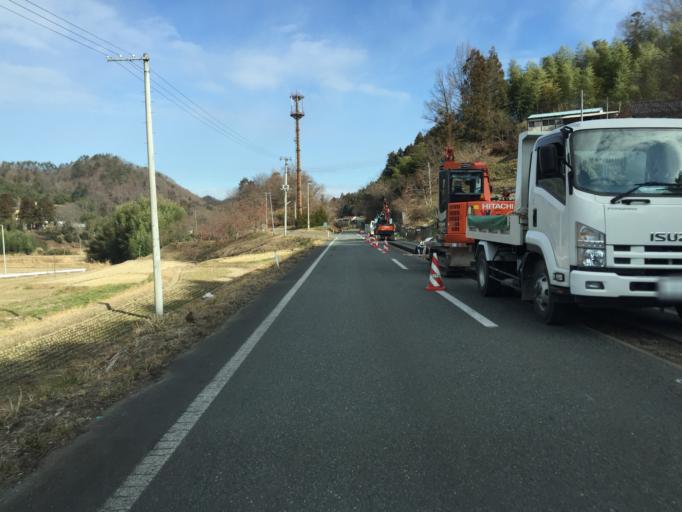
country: JP
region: Fukushima
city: Hobaramachi
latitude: 37.7333
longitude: 140.5559
